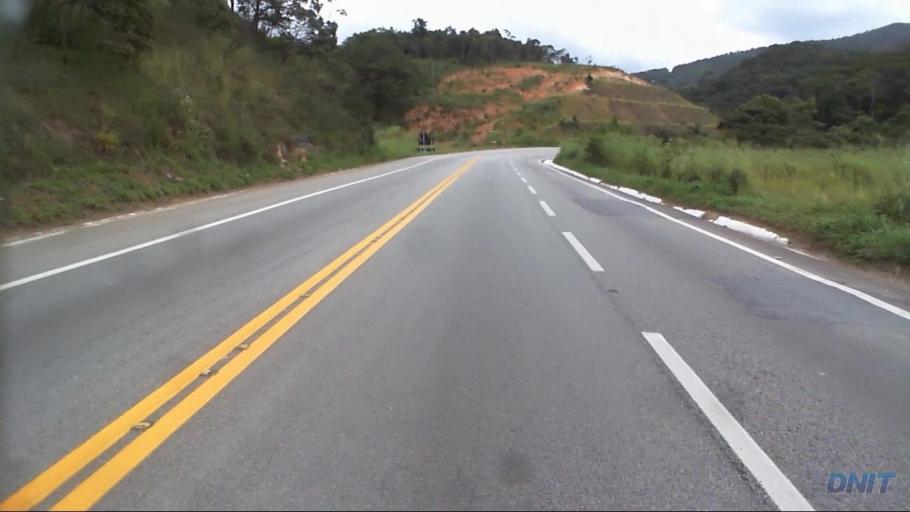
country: BR
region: Minas Gerais
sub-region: Caete
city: Caete
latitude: -19.7953
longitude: -43.6758
